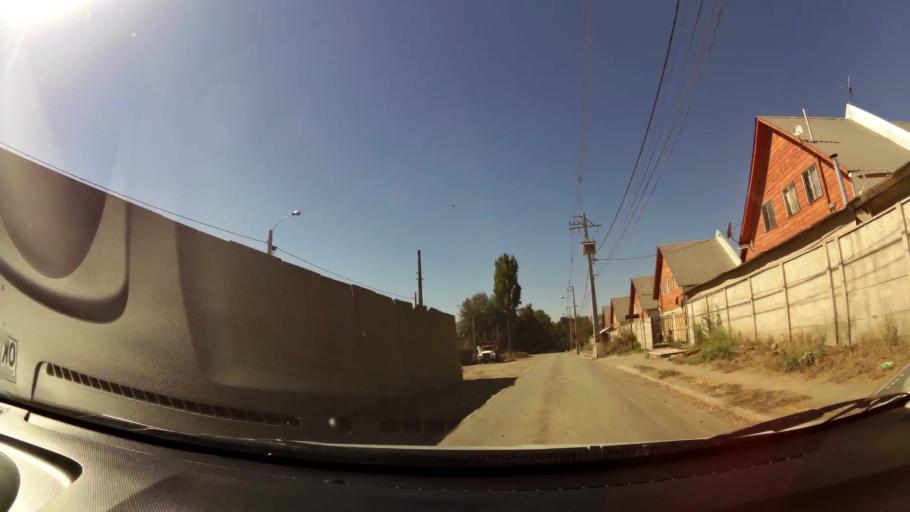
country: CL
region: O'Higgins
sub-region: Provincia de Colchagua
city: Chimbarongo
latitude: -34.5929
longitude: -71.0029
